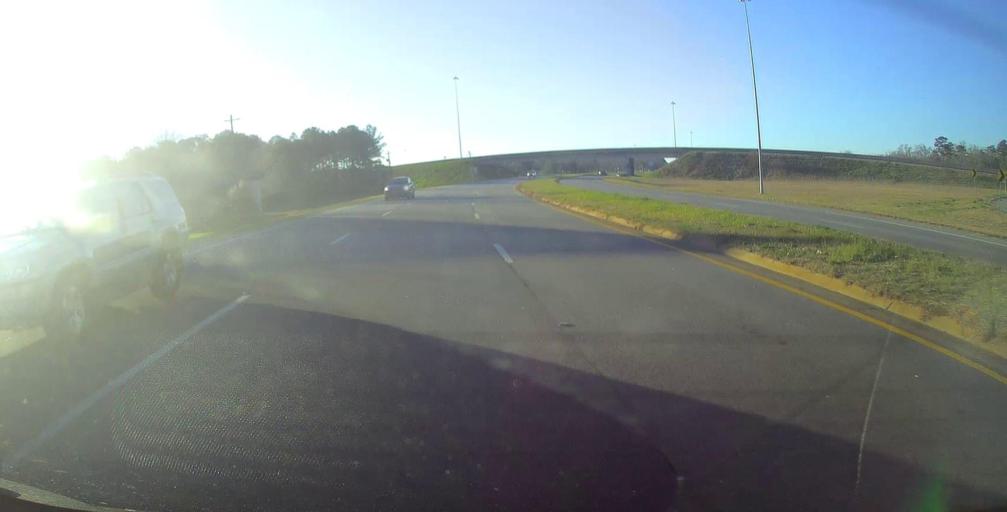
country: US
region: Georgia
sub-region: Dougherty County
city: Albany
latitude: 31.6210
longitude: -84.2283
